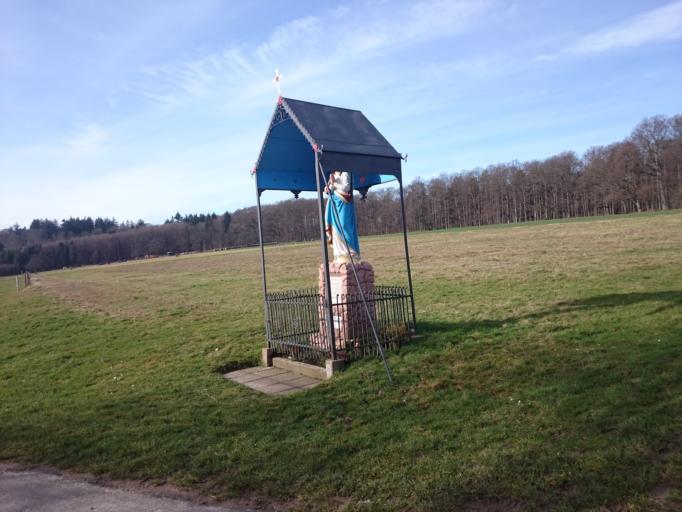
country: DE
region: Baden-Wuerttemberg
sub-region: Karlsruhe Region
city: Ettlingen
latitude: 48.8850
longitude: 8.3979
